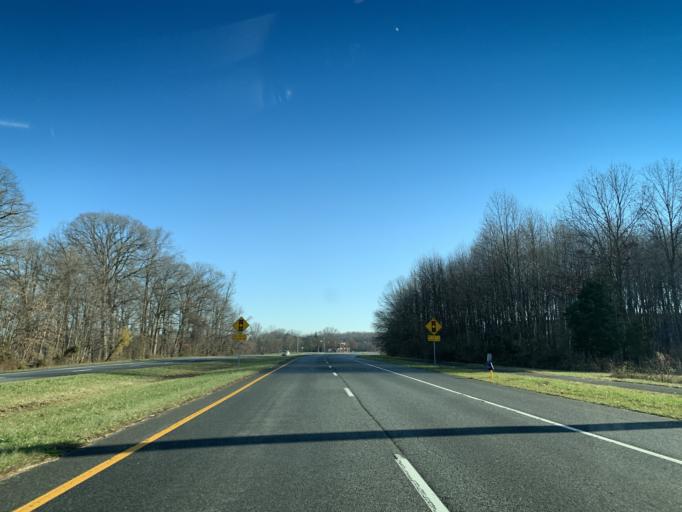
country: US
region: Delaware
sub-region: New Castle County
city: Newport
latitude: 39.6964
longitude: -75.6598
